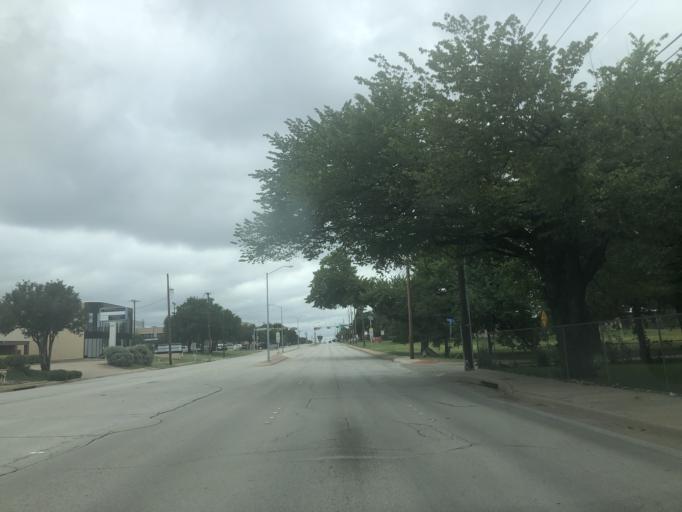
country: US
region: Texas
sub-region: Dallas County
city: Duncanville
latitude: 32.6570
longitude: -96.9256
